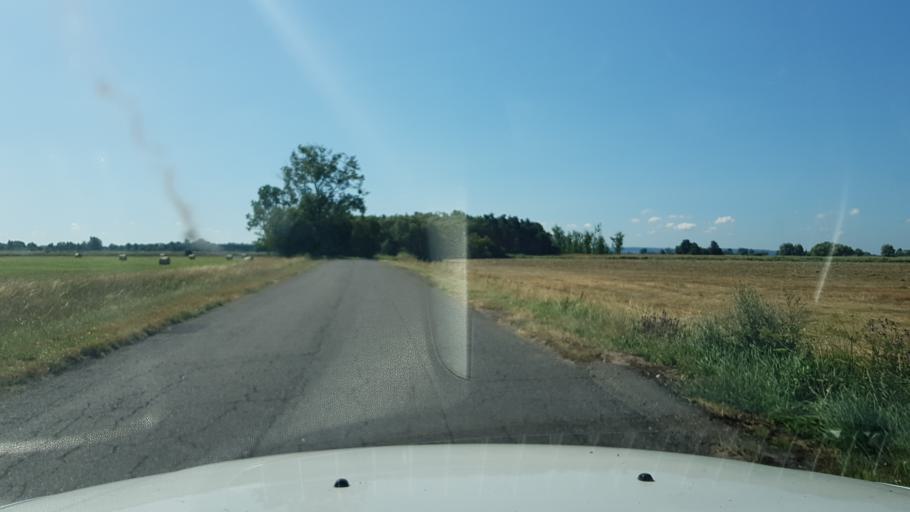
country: PL
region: West Pomeranian Voivodeship
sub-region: Powiat goleniowski
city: Goleniow
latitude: 53.4869
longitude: 14.7115
